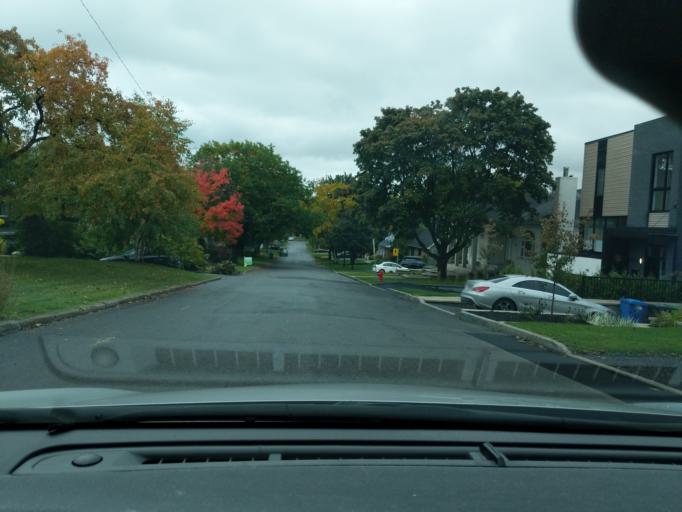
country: CA
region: Quebec
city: Quebec
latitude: 46.7656
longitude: -71.2736
